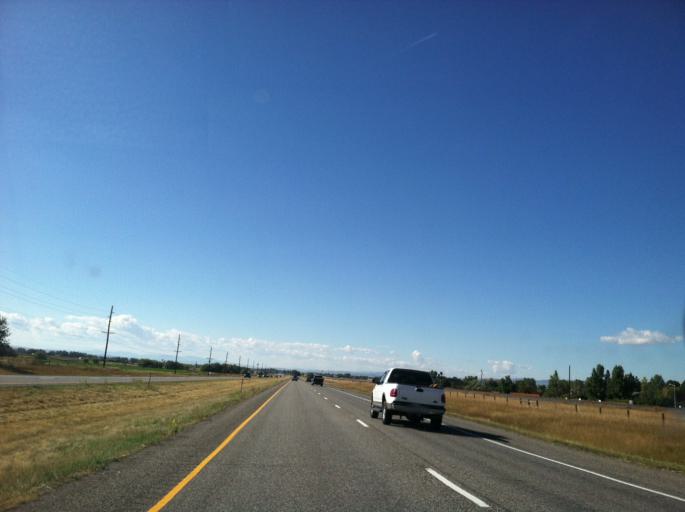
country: US
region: Montana
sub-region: Gallatin County
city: Belgrade
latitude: 45.7379
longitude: -111.1058
